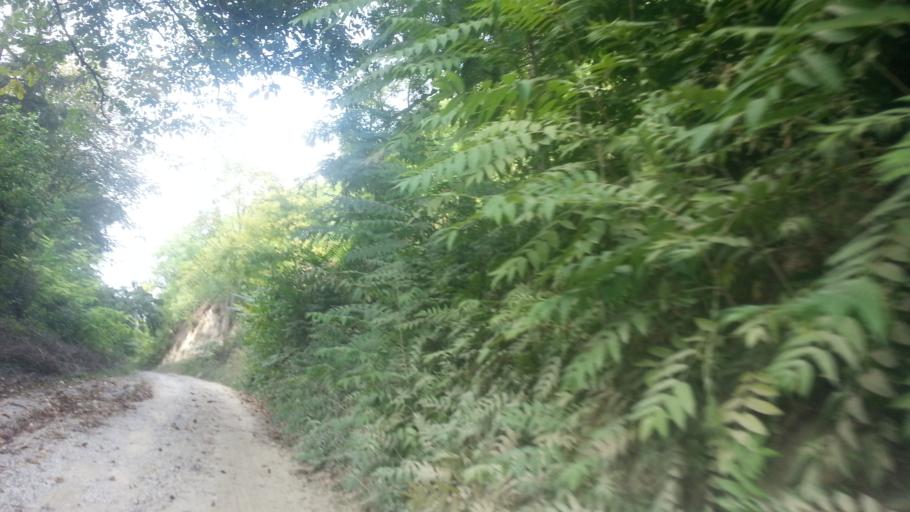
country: RS
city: Belegis
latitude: 45.0207
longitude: 20.3472
